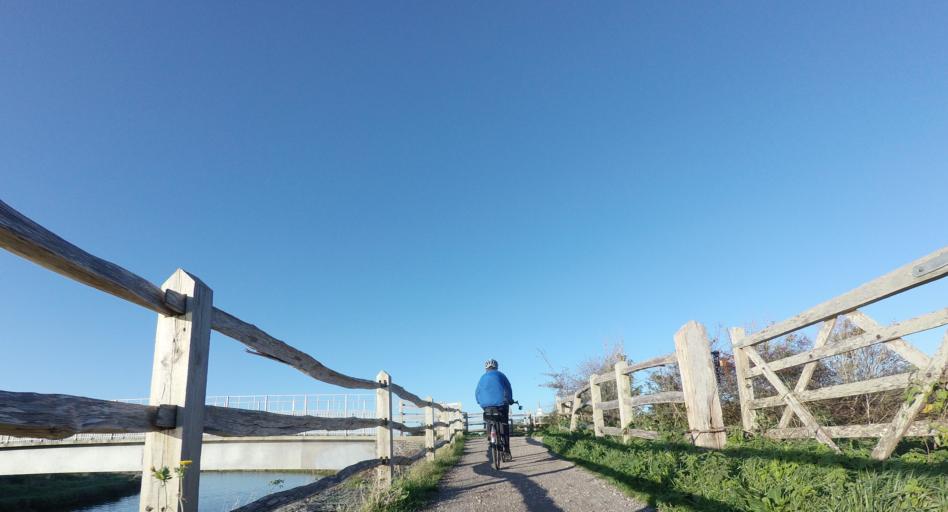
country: GB
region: England
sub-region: West Sussex
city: Steyning
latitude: 50.8706
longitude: -0.3009
